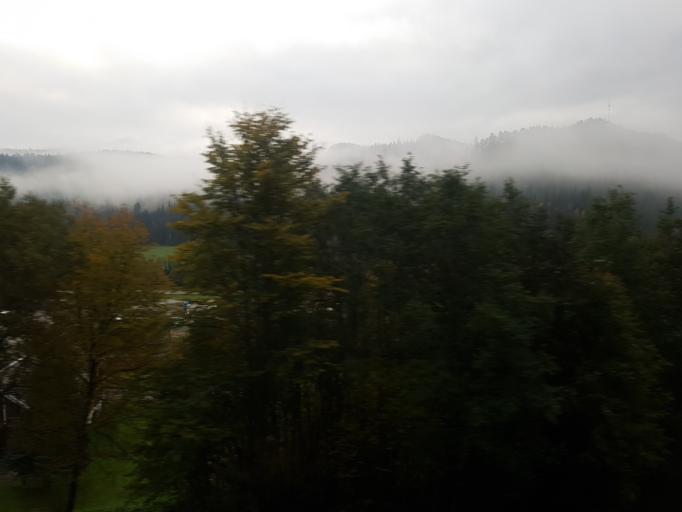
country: NO
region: Sor-Trondelag
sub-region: Midtre Gauldal
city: Storen
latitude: 63.0271
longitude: 10.2627
